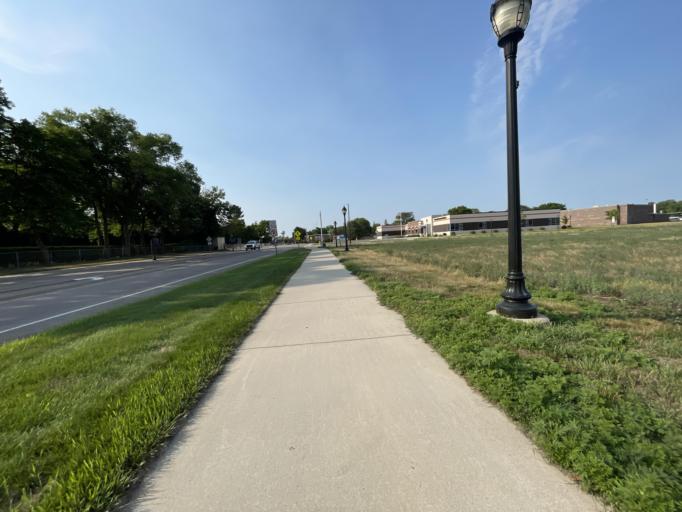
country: US
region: Minnesota
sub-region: Stearns County
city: Saint Joseph
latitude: 45.5609
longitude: -94.3167
